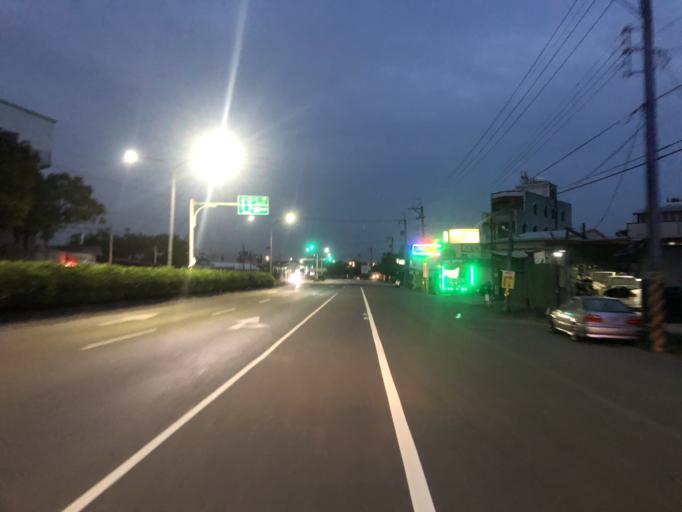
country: TW
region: Taiwan
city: Yujing
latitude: 23.1584
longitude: 120.3399
